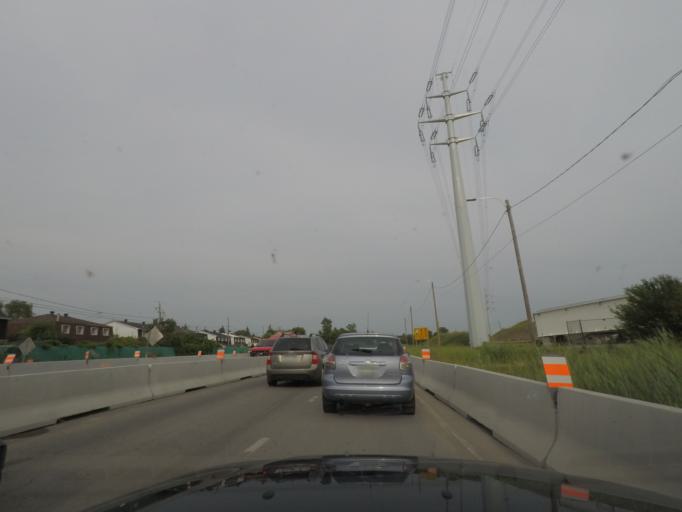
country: CA
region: Quebec
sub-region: Monteregie
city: Brossard
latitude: 45.4676
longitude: -73.4889
